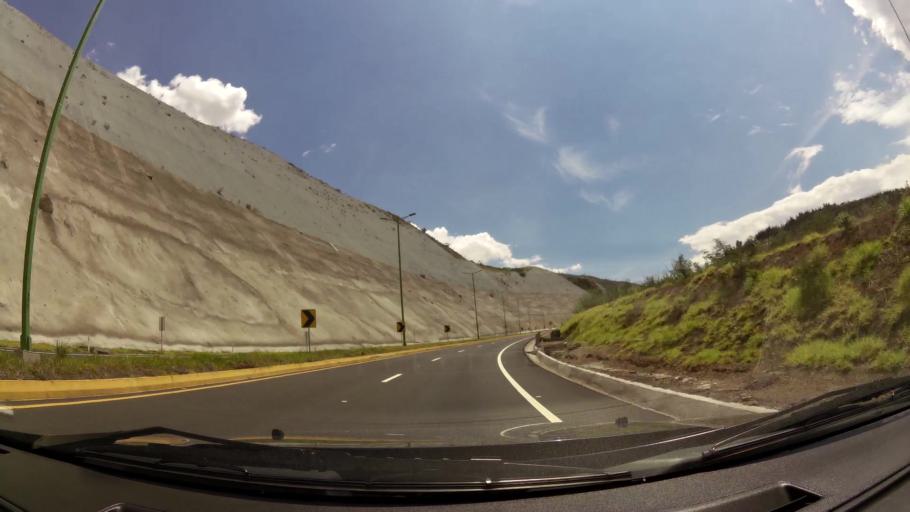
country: EC
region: Pichincha
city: Quito
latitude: -0.0979
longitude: -78.3899
